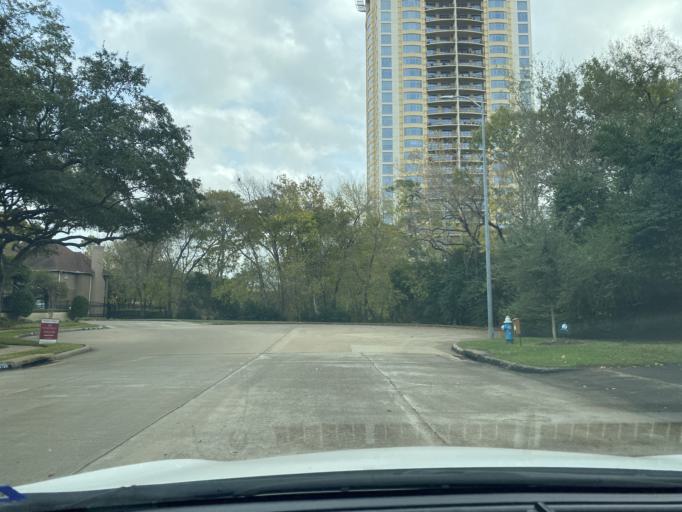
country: US
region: Texas
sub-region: Harris County
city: Hunters Creek Village
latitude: 29.7589
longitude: -95.4592
